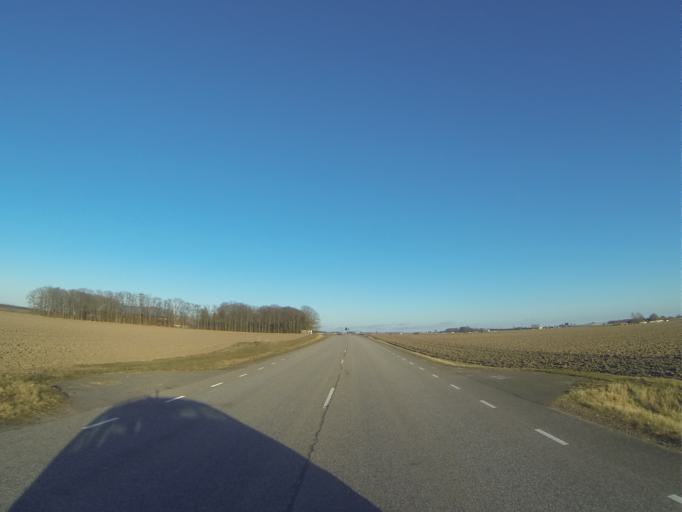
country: SE
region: Skane
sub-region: Malmo
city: Tygelsjo
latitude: 55.5435
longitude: 12.9965
